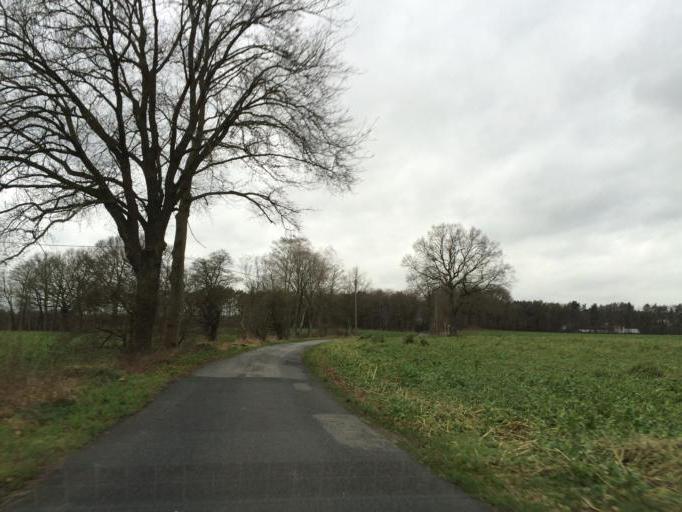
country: DE
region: North Rhine-Westphalia
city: Marl
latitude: 51.7039
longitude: 7.0720
